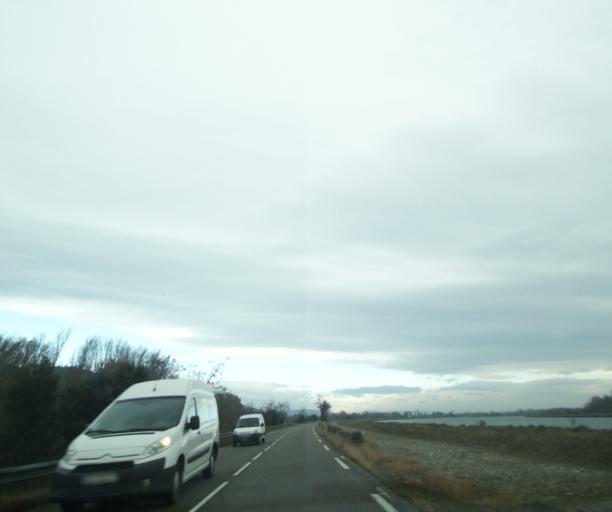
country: FR
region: Rhone-Alpes
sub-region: Departement de l'Ardeche
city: Cornas
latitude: 44.9756
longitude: 4.8568
